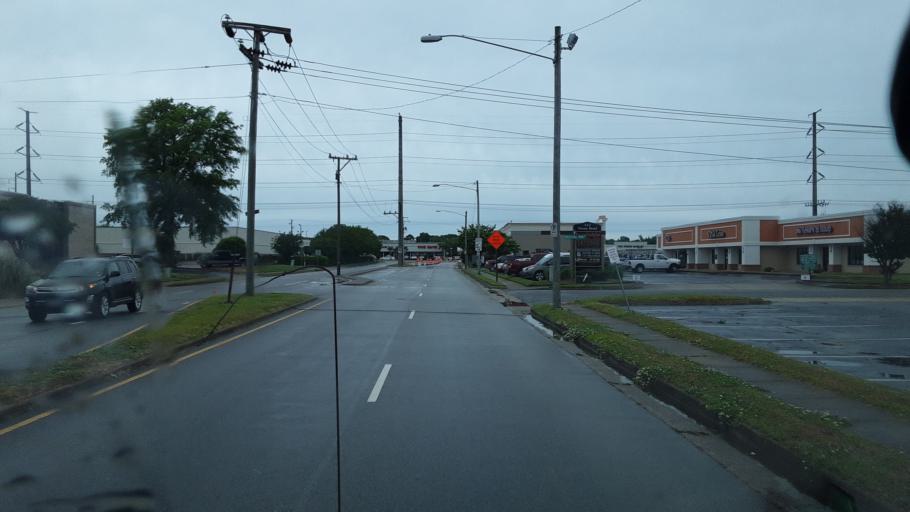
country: US
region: Virginia
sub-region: City of Virginia Beach
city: Virginia Beach
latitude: 36.8491
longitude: -76.0199
